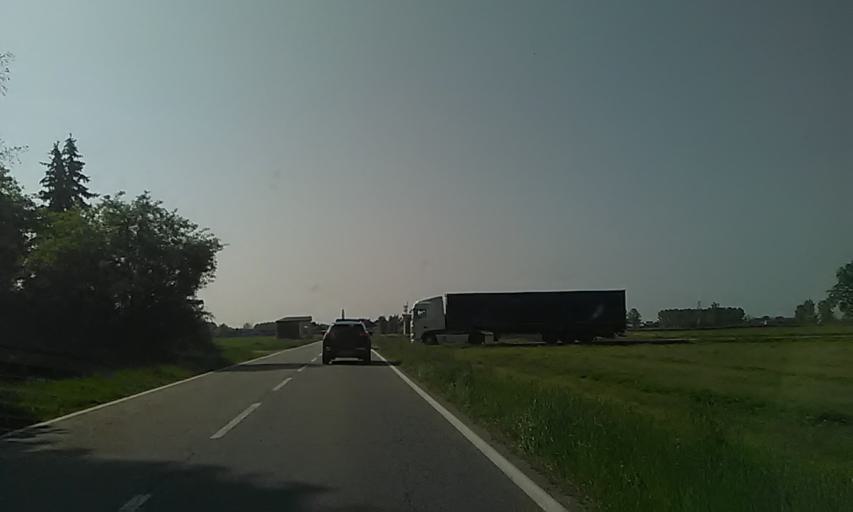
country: IT
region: Piedmont
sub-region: Provincia di Vercelli
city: Arborio
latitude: 45.5086
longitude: 8.3882
